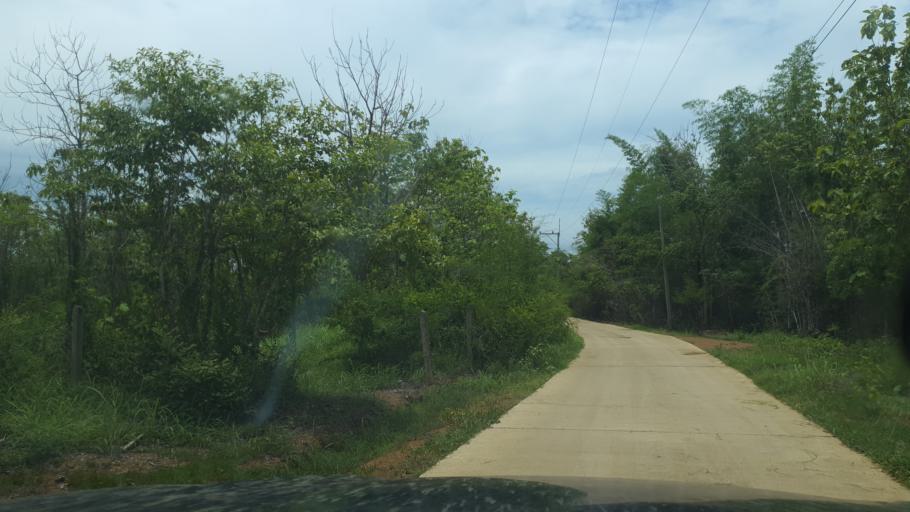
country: TH
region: Lampang
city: Ko Kha
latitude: 18.1331
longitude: 99.3330
